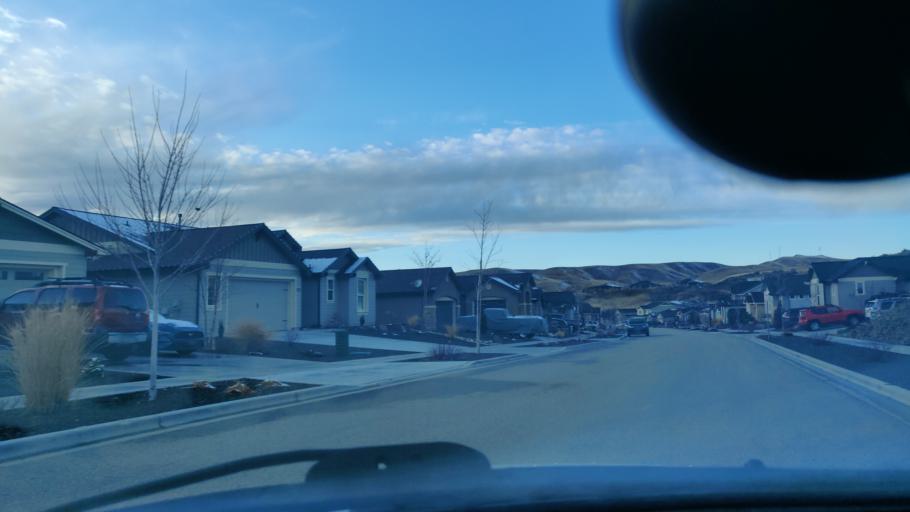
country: US
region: Idaho
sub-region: Ada County
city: Eagle
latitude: 43.7730
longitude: -116.2543
